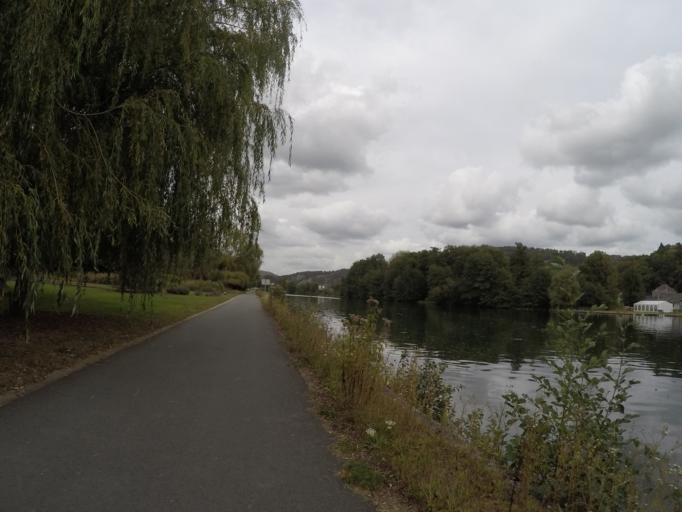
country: BE
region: Wallonia
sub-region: Province de Namur
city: Yvoir
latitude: 50.3207
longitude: 4.8748
